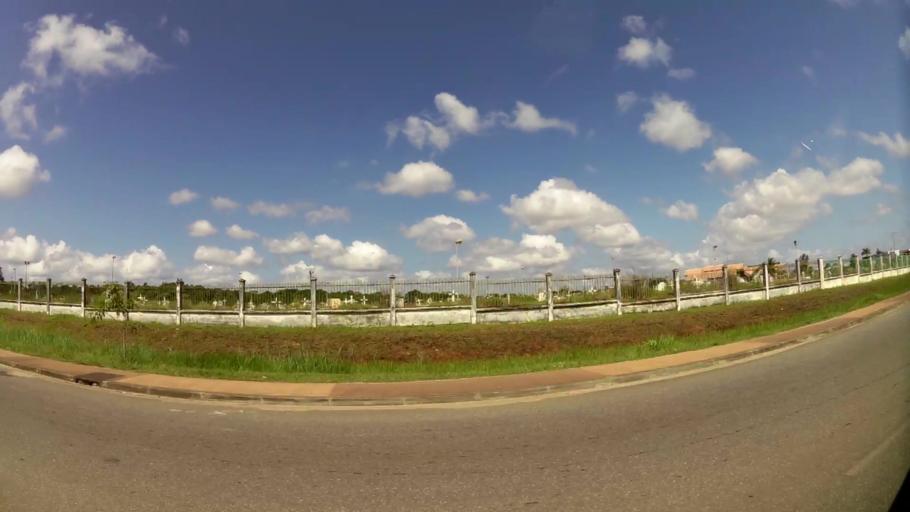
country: GF
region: Guyane
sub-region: Guyane
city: Cayenne
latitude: 4.9166
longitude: -52.3120
